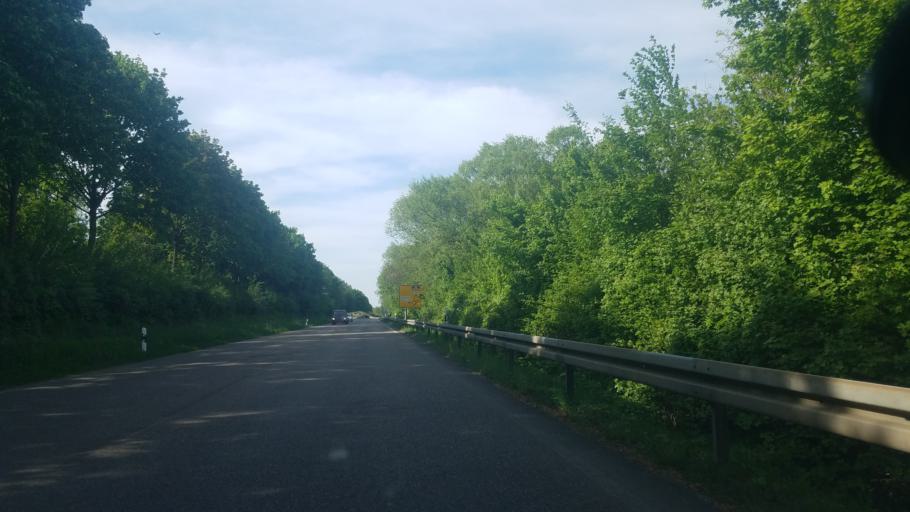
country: DE
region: Baden-Wuerttemberg
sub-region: Freiburg Region
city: Kehl
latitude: 48.5609
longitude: 7.8385
